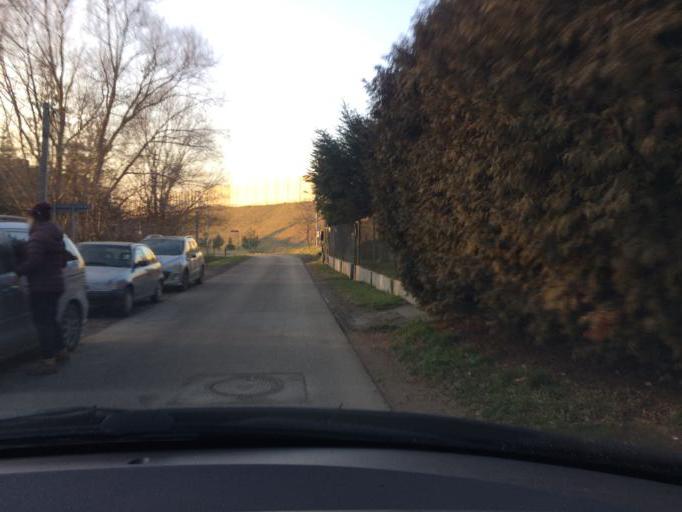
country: PL
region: Lesser Poland Voivodeship
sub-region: Powiat wielicki
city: Czarnochowice
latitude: 50.0054
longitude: 20.0365
